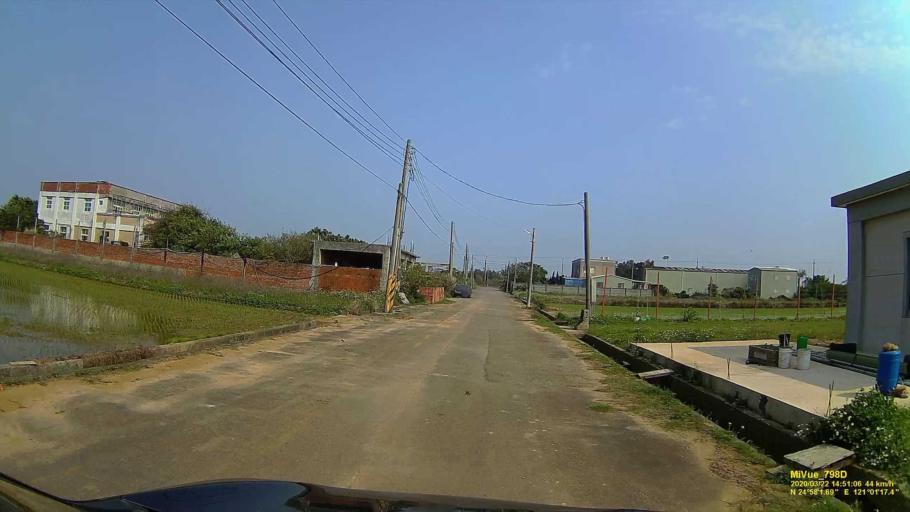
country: TW
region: Taiwan
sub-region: Hsinchu
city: Zhubei
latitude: 24.9671
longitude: 121.0216
